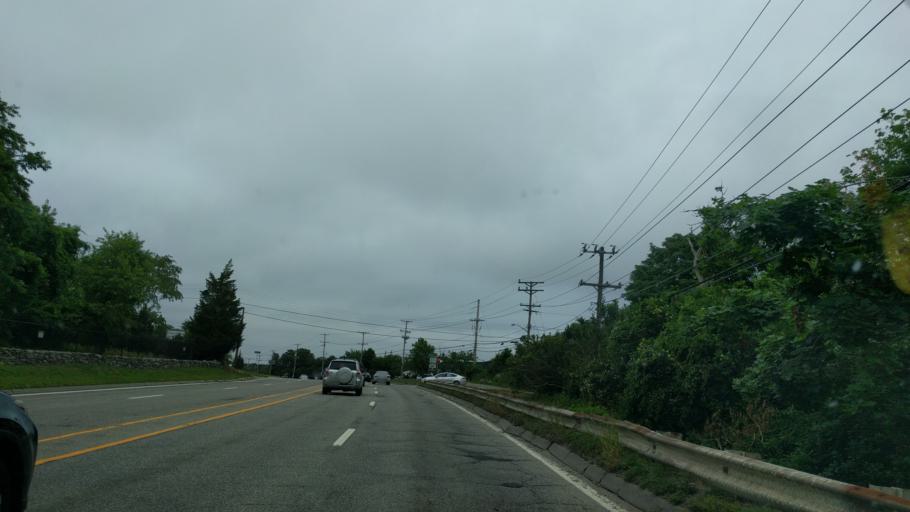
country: US
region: Rhode Island
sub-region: Newport County
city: Melville
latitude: 41.5737
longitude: -71.2731
